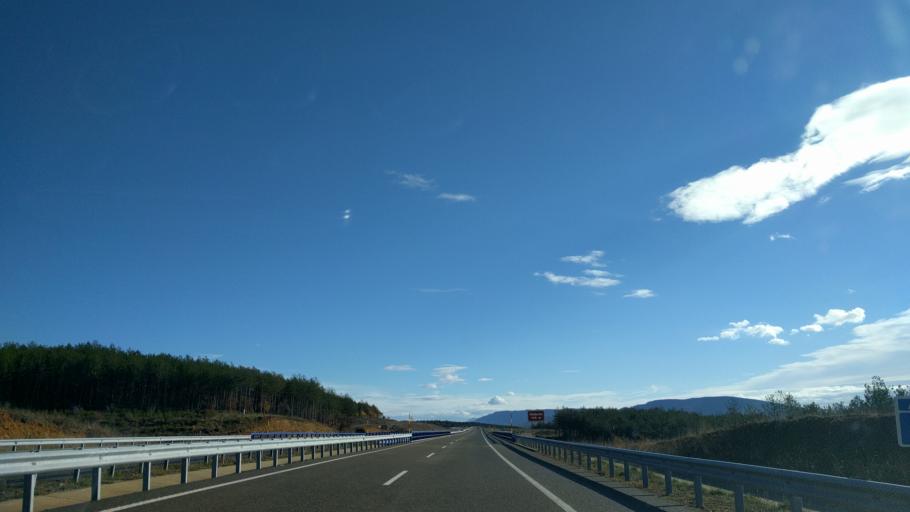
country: ES
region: Navarre
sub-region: Provincia de Navarra
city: Yesa
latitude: 42.6209
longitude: -1.1550
